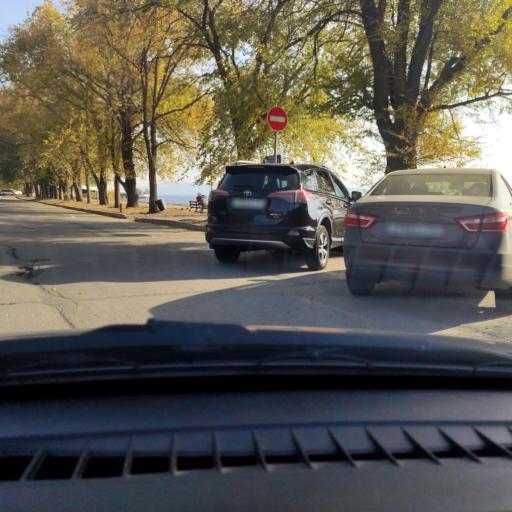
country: RU
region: Samara
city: Tol'yatti
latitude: 53.5023
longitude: 49.2507
